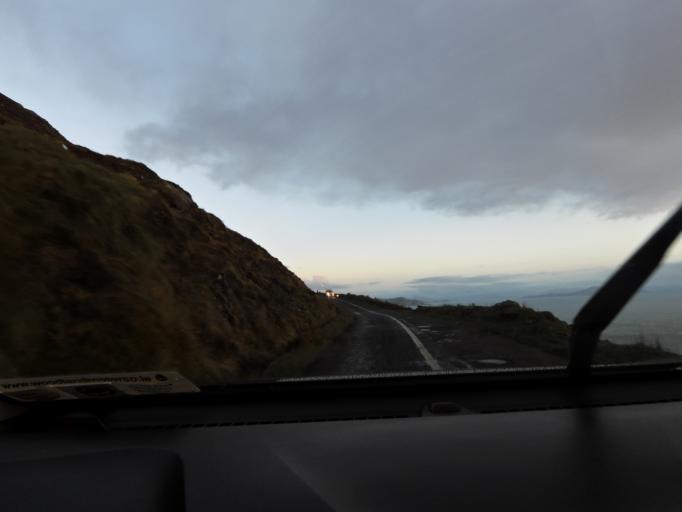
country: IE
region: Connaught
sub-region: Maigh Eo
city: Belmullet
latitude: 53.9702
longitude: -10.1783
